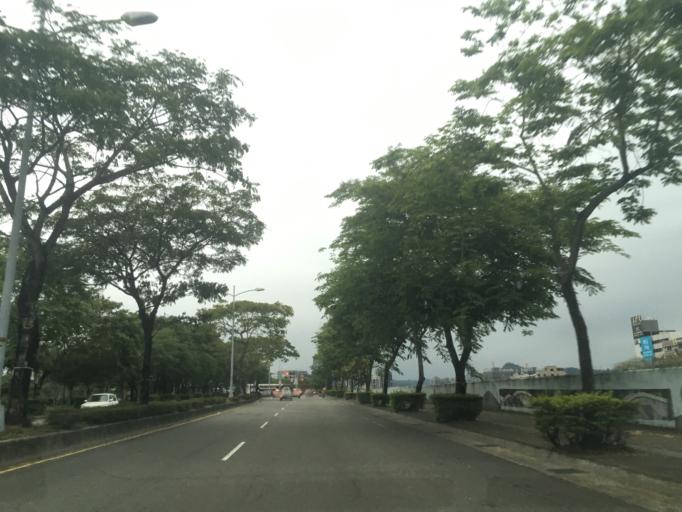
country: TW
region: Taiwan
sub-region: Taichung City
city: Taichung
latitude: 24.1472
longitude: 120.7227
